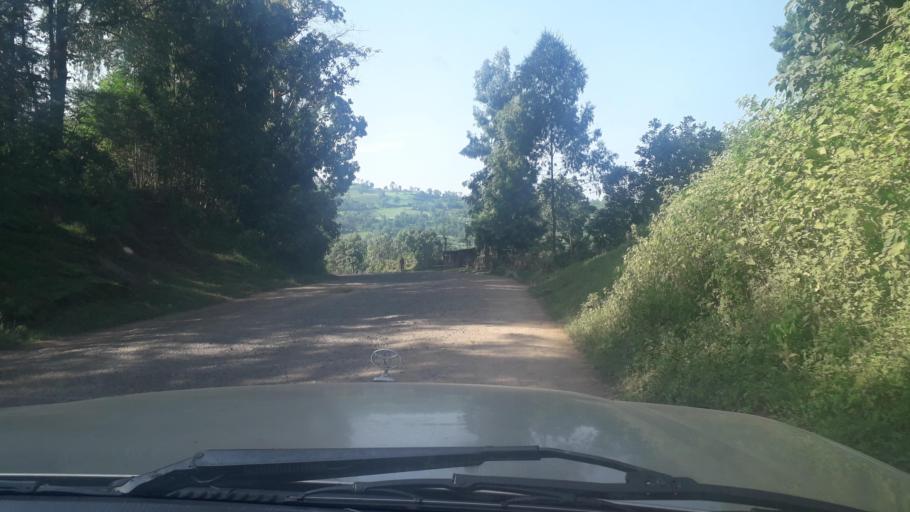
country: ET
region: Oromiya
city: Jima
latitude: 7.3816
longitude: 36.8689
